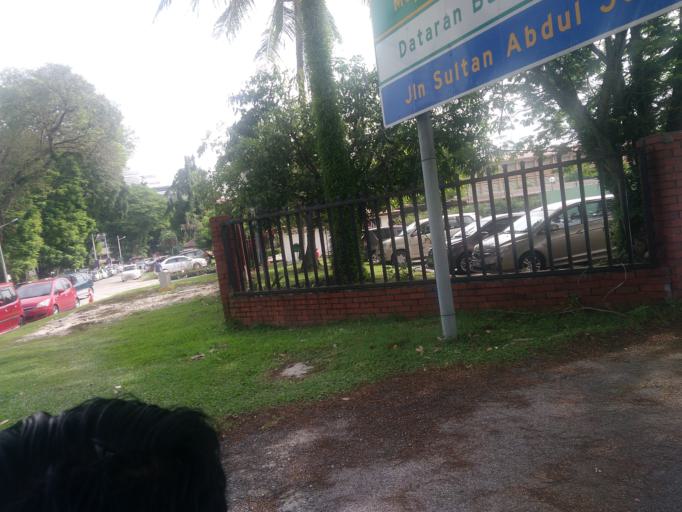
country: MY
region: Perak
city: Ipoh
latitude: 4.5997
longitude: 101.0895
